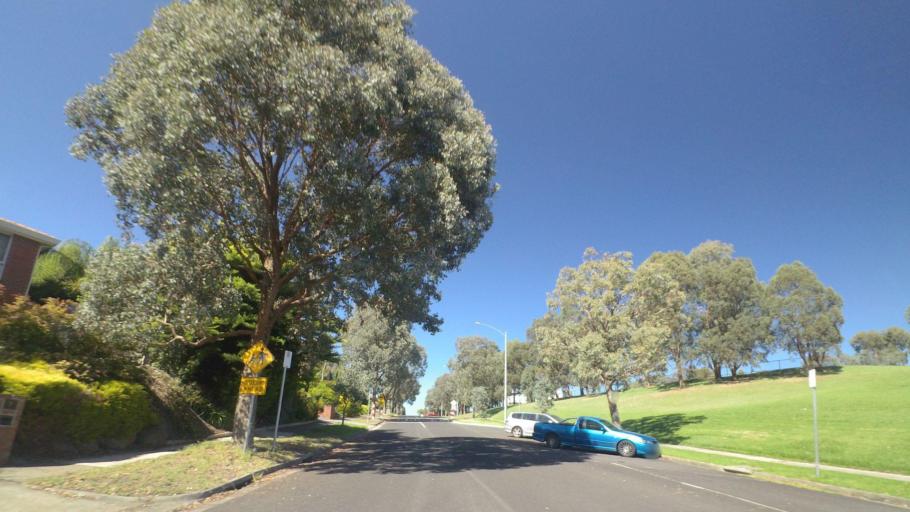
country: AU
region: Victoria
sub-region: Manningham
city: Donvale
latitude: -37.7718
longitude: 145.1753
